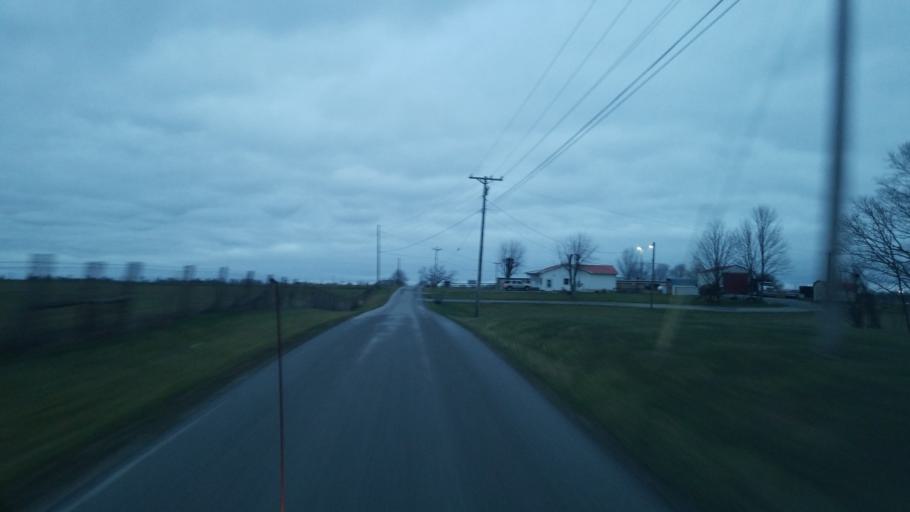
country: US
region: Kentucky
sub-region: Fleming County
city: Flemingsburg
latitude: 38.4896
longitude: -83.6583
